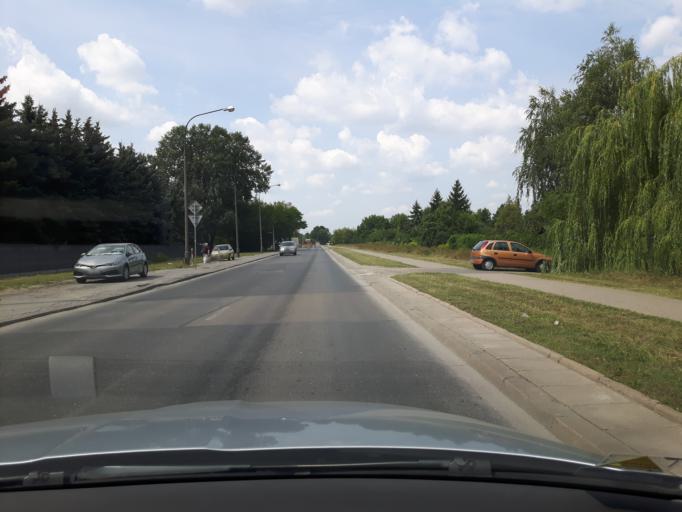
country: PL
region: Masovian Voivodeship
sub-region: Warszawa
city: Wilanow
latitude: 52.1905
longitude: 21.0824
